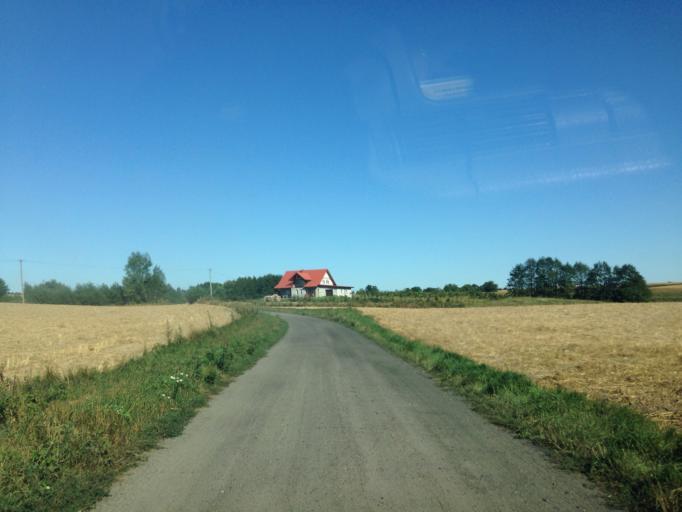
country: PL
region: Kujawsko-Pomorskie
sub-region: Powiat brodnicki
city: Brodnica
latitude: 53.2108
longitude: 19.4625
